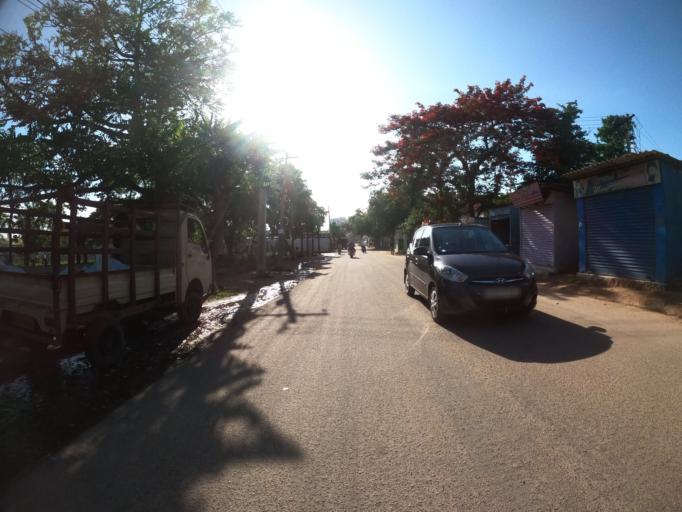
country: IN
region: Telangana
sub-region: Hyderabad
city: Hyderabad
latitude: 17.3546
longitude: 78.3784
